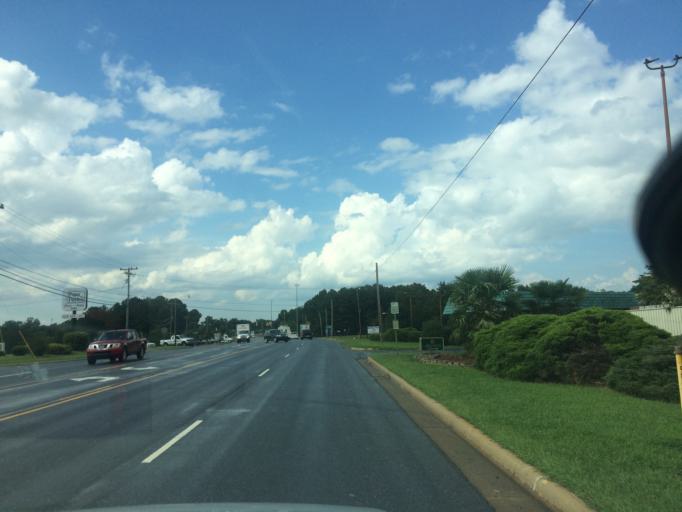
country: US
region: North Carolina
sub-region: Catawba County
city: Conover
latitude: 35.7000
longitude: -81.2618
